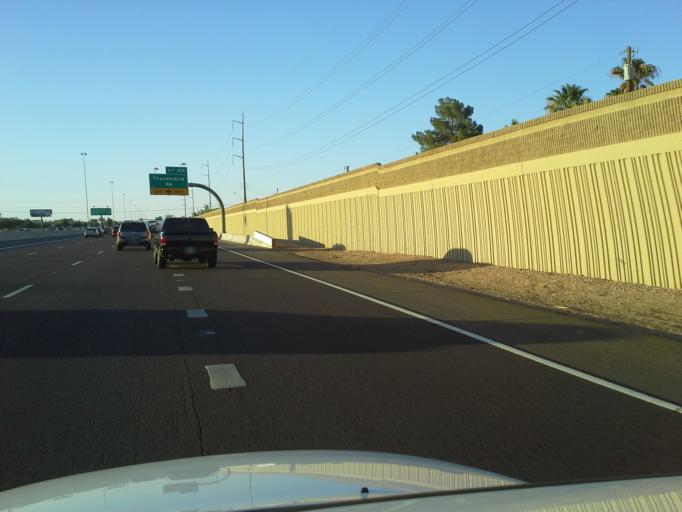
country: US
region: Arizona
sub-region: Maricopa County
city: Glendale
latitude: 33.6013
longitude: -112.1166
